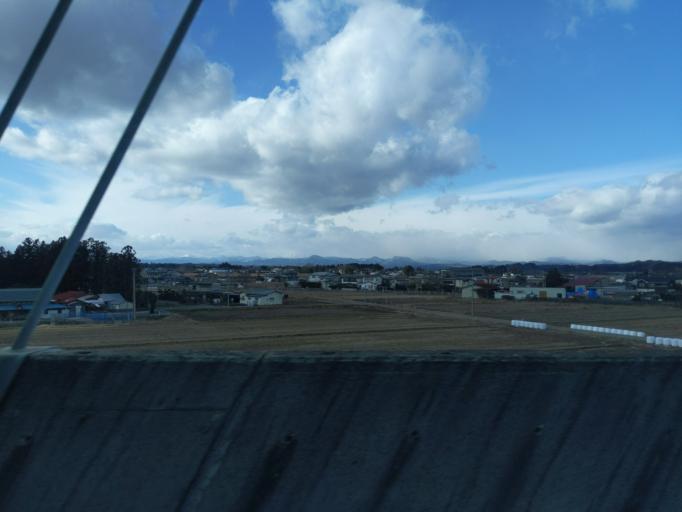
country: JP
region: Iwate
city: Ichinoseki
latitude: 38.7566
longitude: 141.0760
